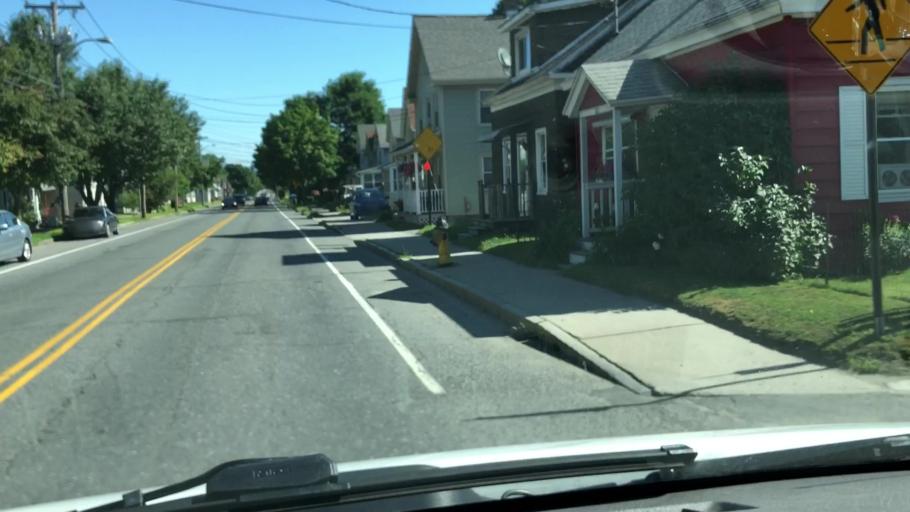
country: US
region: Massachusetts
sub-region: Berkshire County
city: Adams
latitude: 42.6310
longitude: -73.1146
